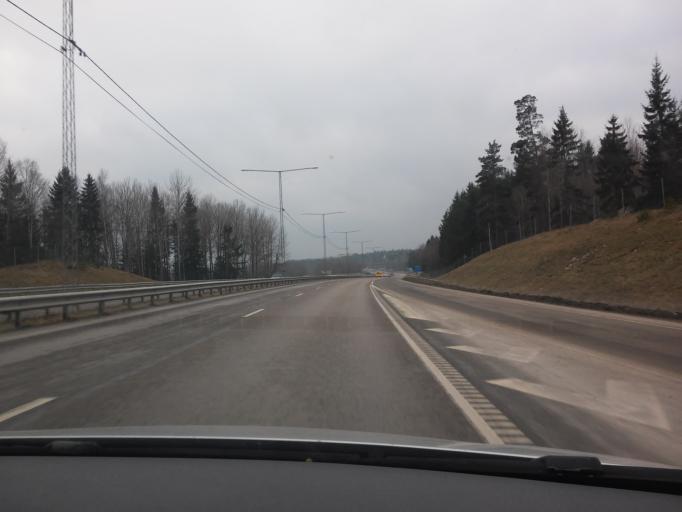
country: SE
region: Stockholm
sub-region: Taby Kommun
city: Taby
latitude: 59.4634
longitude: 18.1471
